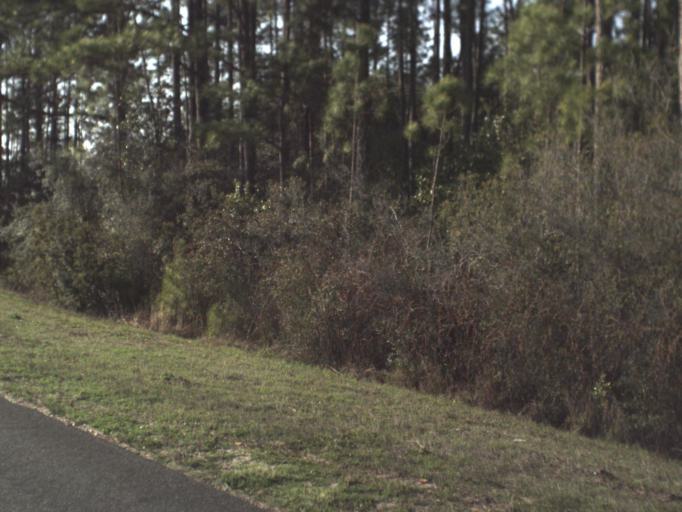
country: US
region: Florida
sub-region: Bay County
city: Lynn Haven
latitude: 30.4398
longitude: -85.7832
